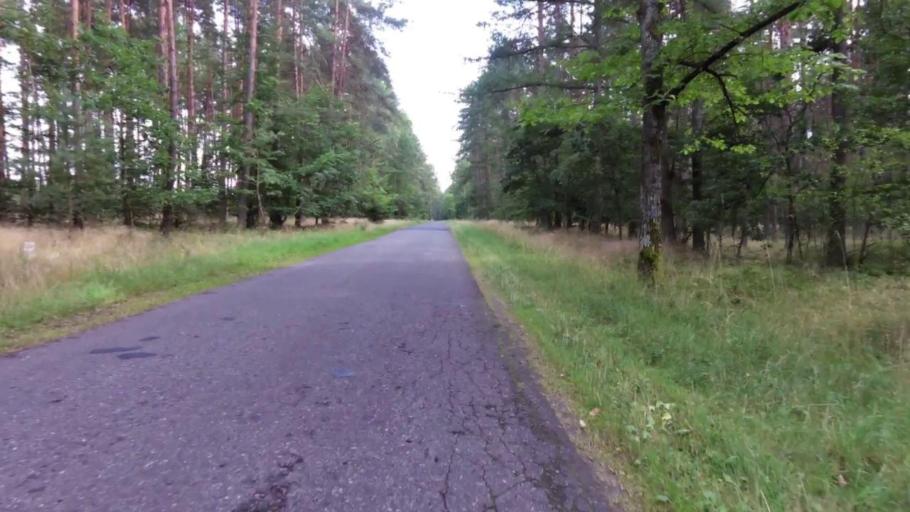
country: PL
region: West Pomeranian Voivodeship
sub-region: Powiat drawski
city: Zlocieniec
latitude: 53.5538
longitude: 15.9899
